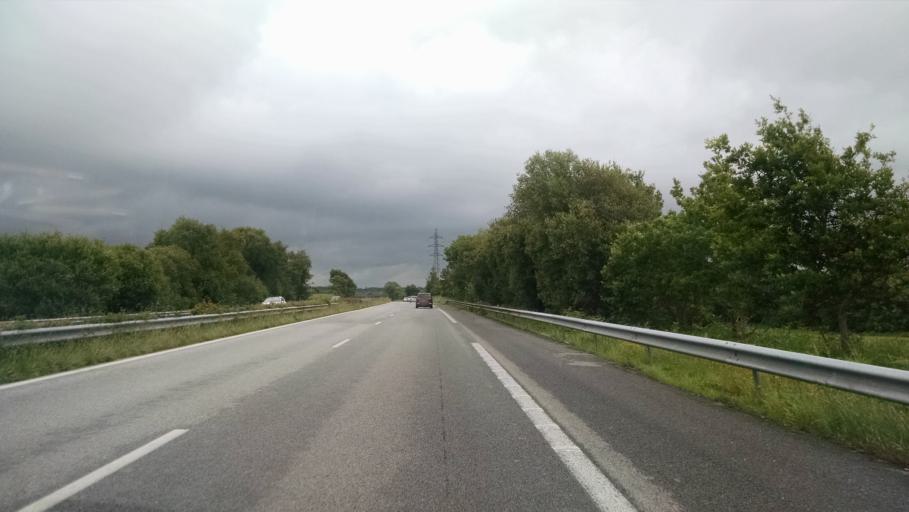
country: FR
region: Brittany
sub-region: Departement du Finistere
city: Melgven
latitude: 47.9002
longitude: -3.8373
